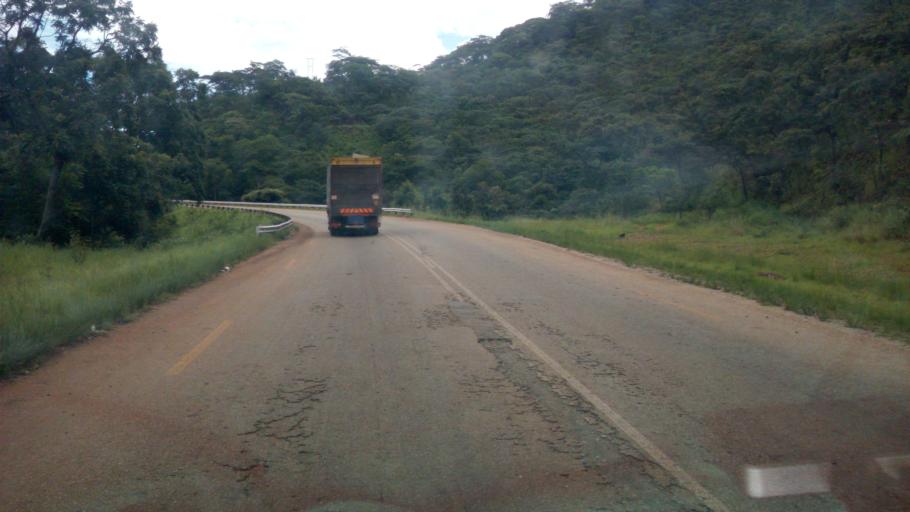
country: ZW
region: Mashonaland Central
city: Mazowe
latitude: -17.5197
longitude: 30.9858
